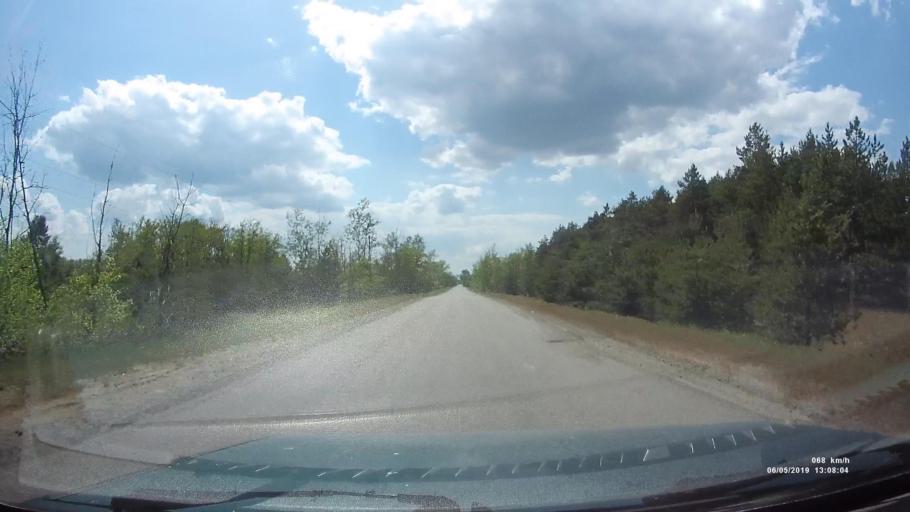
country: RU
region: Rostov
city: Ust'-Donetskiy
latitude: 47.7782
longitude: 40.9994
